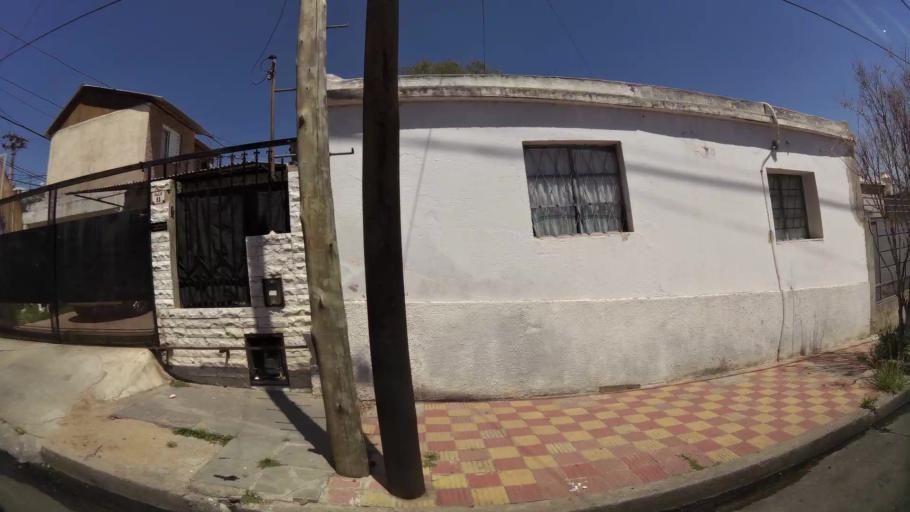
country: AR
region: Cordoba
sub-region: Departamento de Capital
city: Cordoba
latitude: -31.3938
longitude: -64.2001
